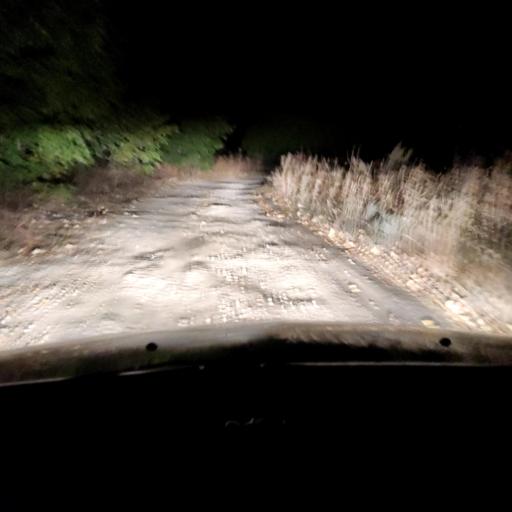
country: RU
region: Voronezj
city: Semiluki
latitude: 51.7198
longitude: 38.9954
